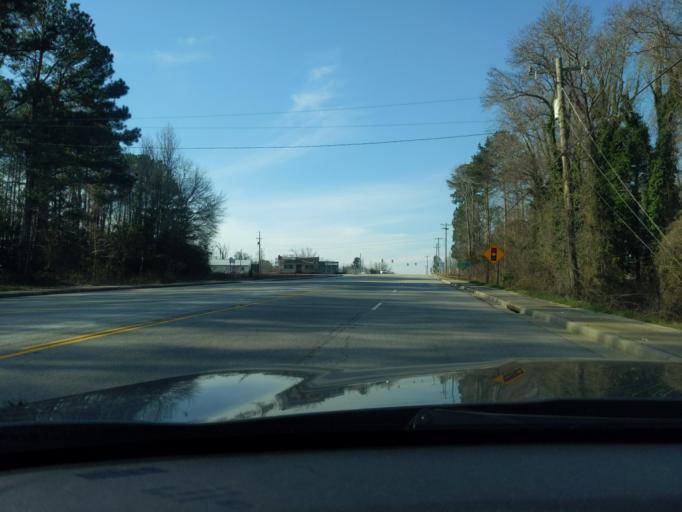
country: US
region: South Carolina
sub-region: Abbeville County
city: Abbeville
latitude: 34.1536
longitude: -82.3931
